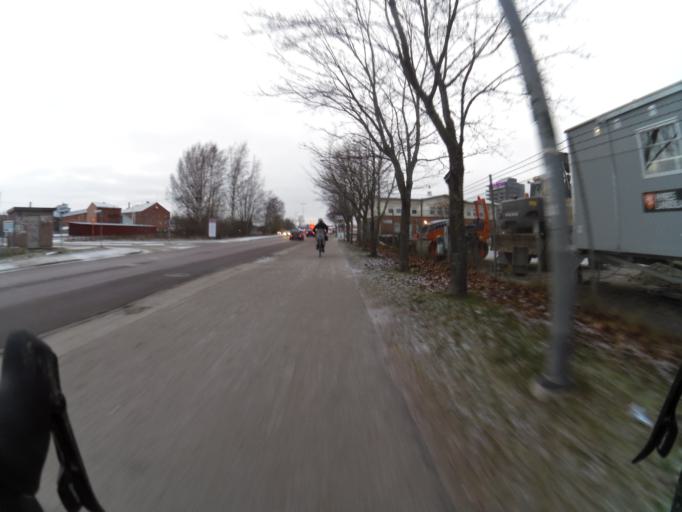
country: SE
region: Gaevleborg
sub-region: Gavle Kommun
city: Gavle
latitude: 60.6780
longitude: 17.1672
